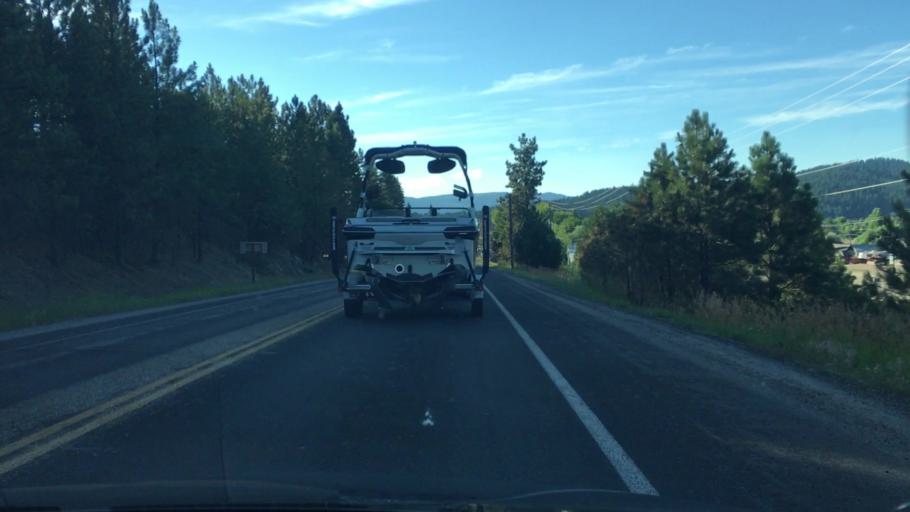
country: US
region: Idaho
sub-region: Valley County
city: Cascade
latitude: 44.5098
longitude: -116.0355
